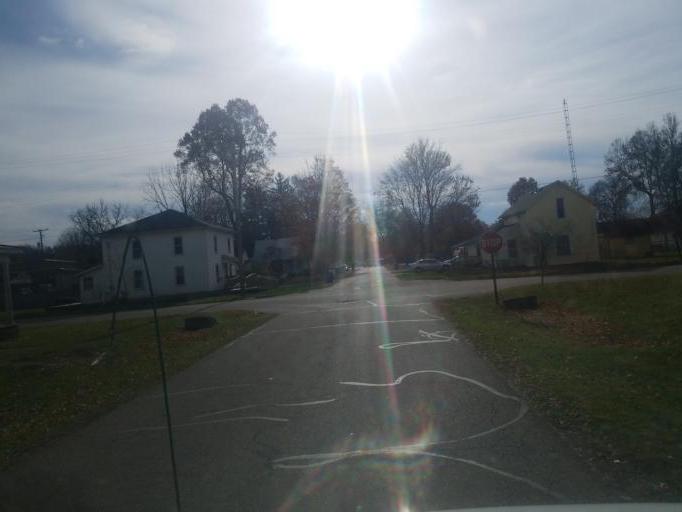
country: US
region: Ohio
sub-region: Knox County
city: Mount Vernon
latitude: 40.4028
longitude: -82.4929
